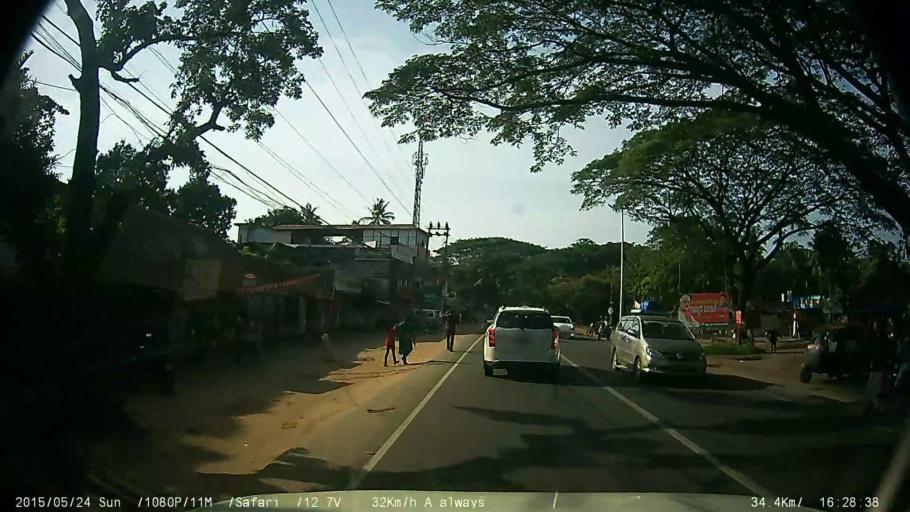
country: IN
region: Kerala
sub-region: Alappuzha
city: Alleppey
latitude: 9.5378
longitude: 76.3272
